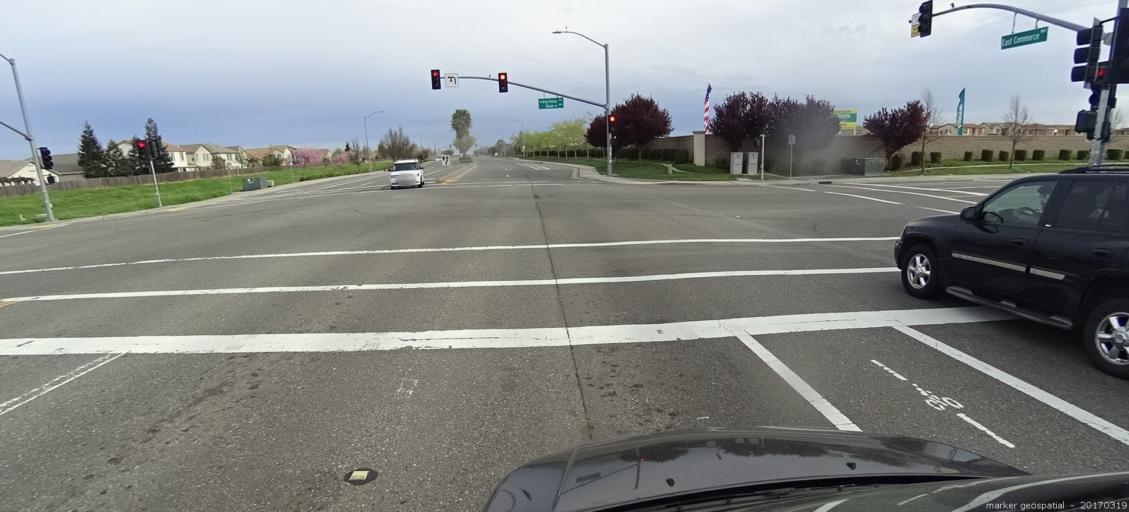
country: US
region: California
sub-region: Sacramento County
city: Elverta
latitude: 38.6799
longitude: -121.5314
